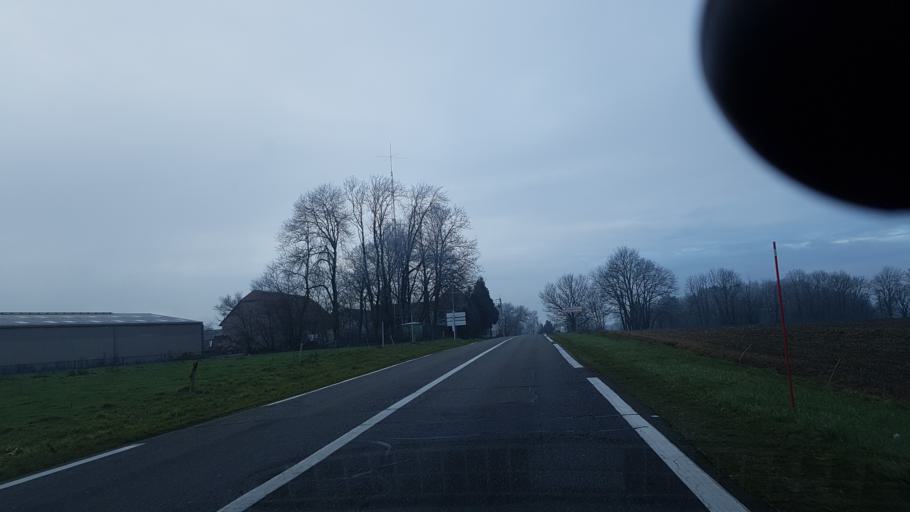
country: FR
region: Lorraine
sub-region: Departement de la Moselle
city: Bitche
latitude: 49.0596
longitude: 7.3958
